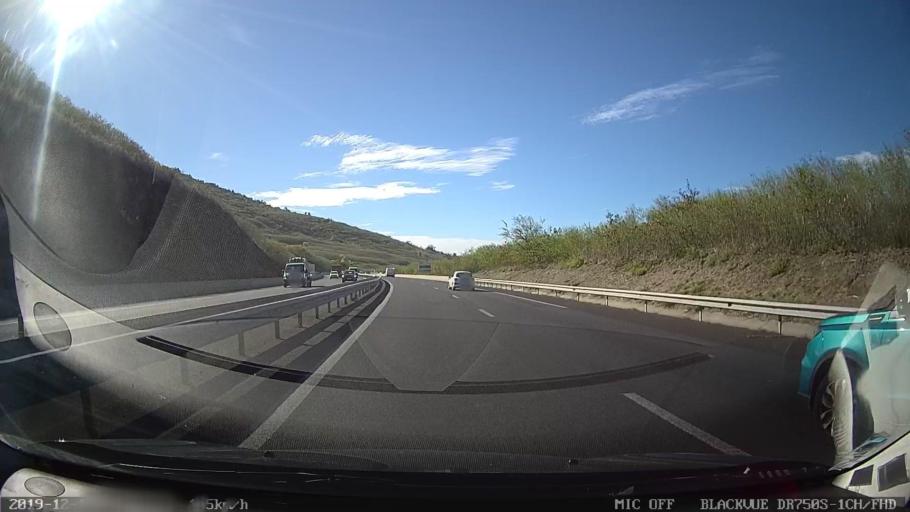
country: RE
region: Reunion
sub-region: Reunion
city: Trois-Bassins
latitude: -21.1309
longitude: 55.2828
